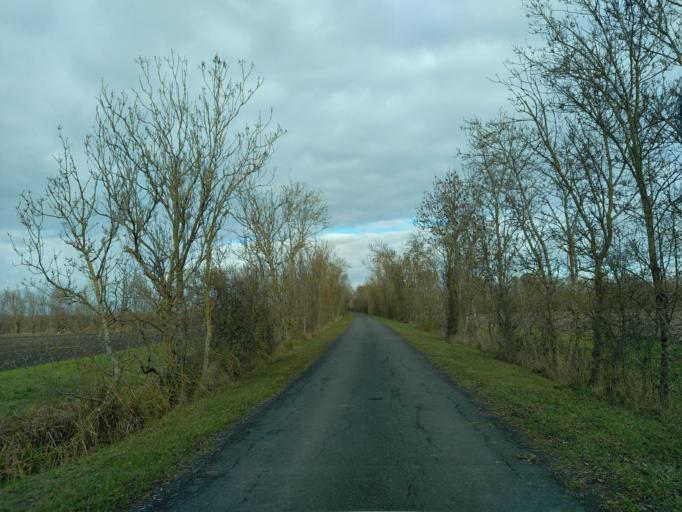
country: FR
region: Pays de la Loire
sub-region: Departement de la Vendee
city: Maillezais
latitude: 46.3299
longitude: -0.7928
